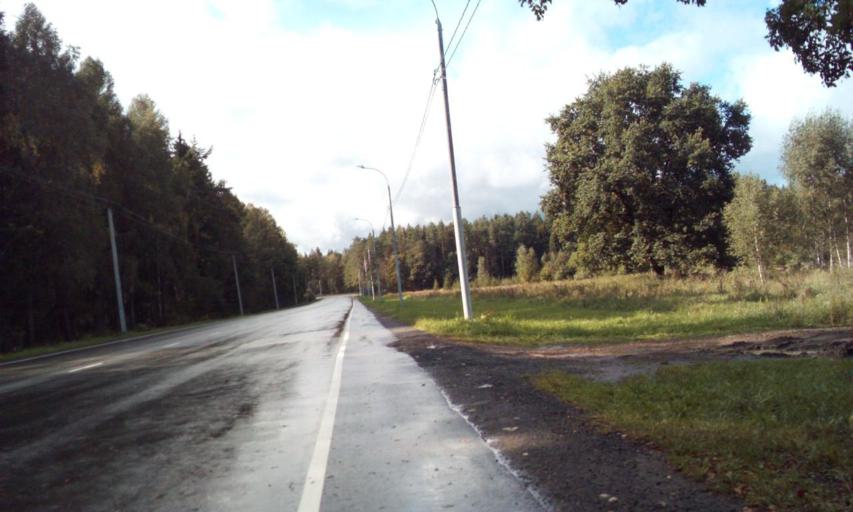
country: RU
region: Moskovskaya
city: Kievskij
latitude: 55.4476
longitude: 36.9008
